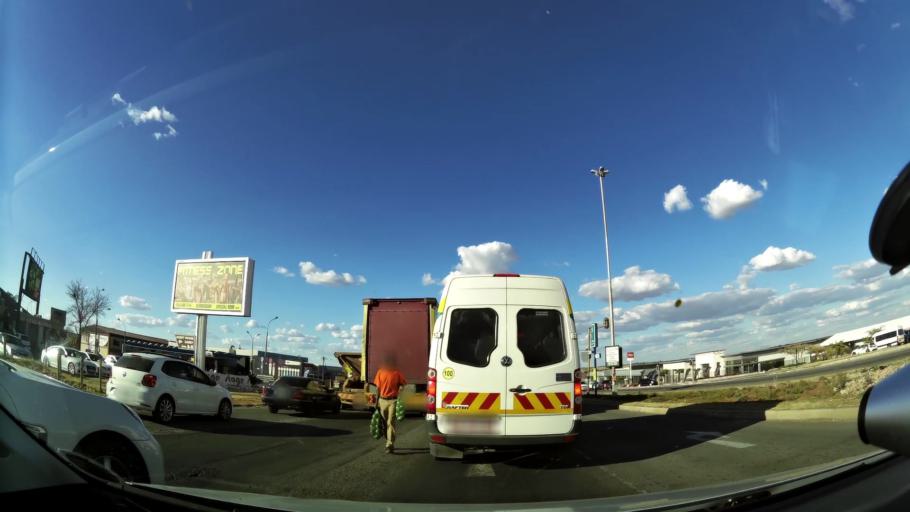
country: ZA
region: North-West
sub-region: Dr Kenneth Kaunda District Municipality
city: Klerksdorp
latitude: -26.8510
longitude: 26.6899
